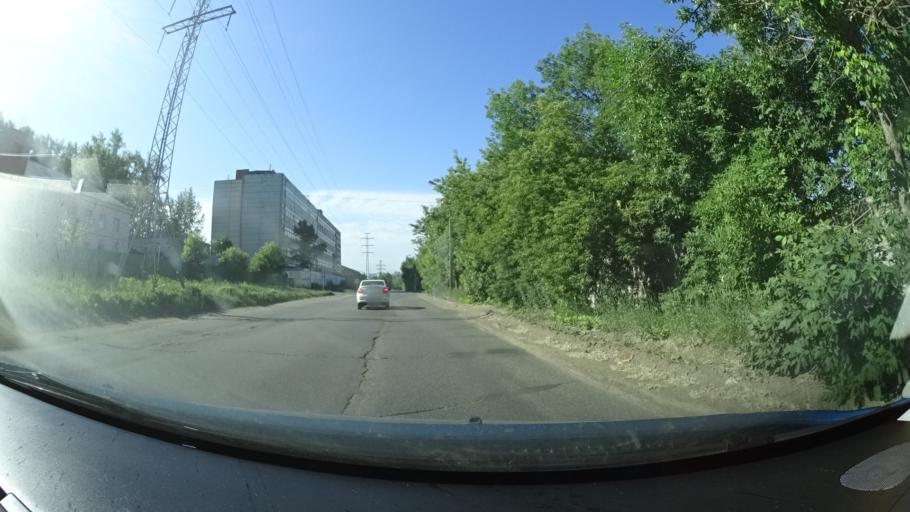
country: RU
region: Bashkortostan
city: Ufa
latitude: 54.8428
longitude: 56.0755
